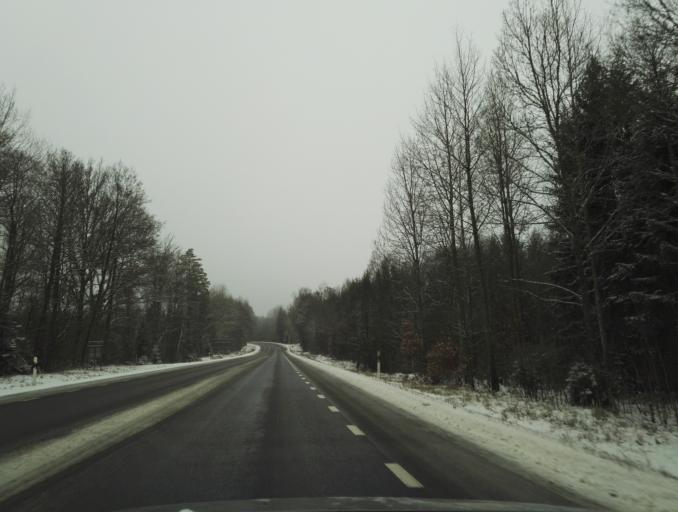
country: SE
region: Kronoberg
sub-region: Vaxjo Kommun
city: Vaexjoe
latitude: 56.8647
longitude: 14.7350
